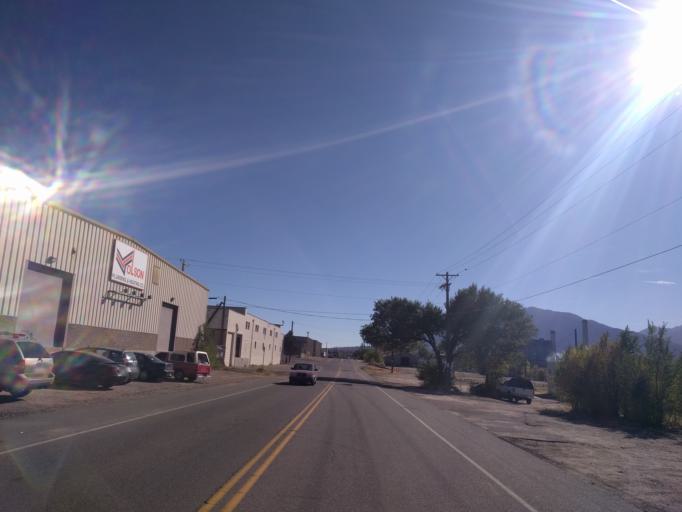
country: US
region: Colorado
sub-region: El Paso County
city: Colorado Springs
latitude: 38.8311
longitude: -104.8291
